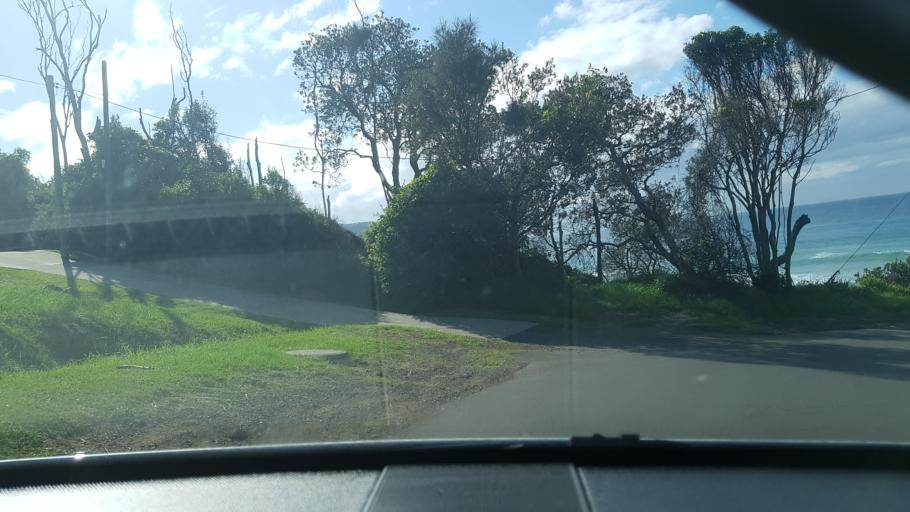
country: AU
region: New South Wales
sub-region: Gosford Shire
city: Macmasters Beach
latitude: -33.4986
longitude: 151.4244
